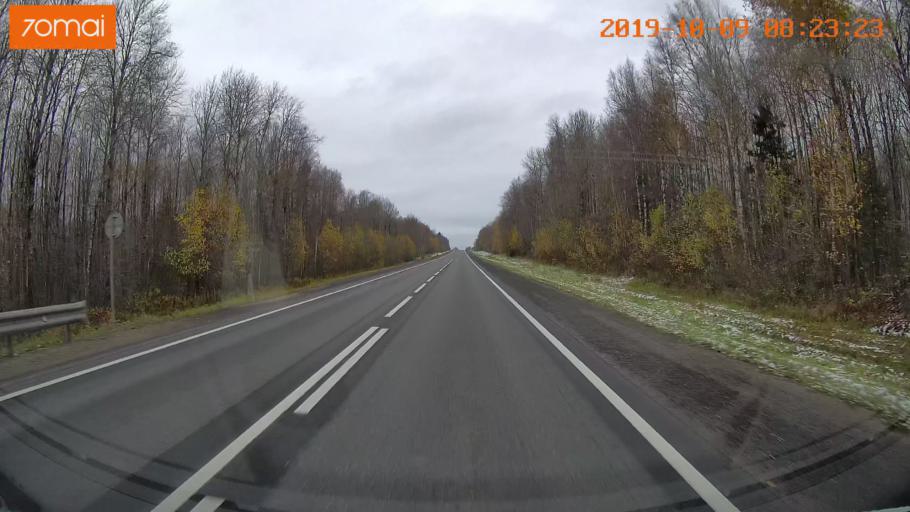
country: RU
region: Vologda
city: Gryazovets
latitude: 58.7537
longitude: 40.2837
